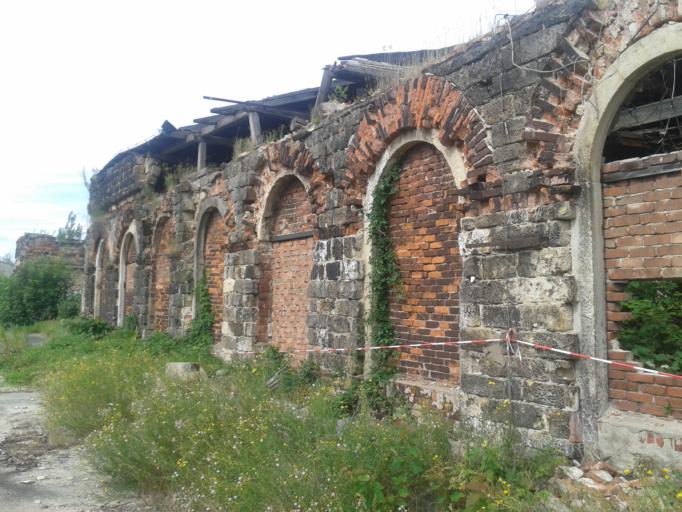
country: DE
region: Saxony
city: Dresden
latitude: 51.0659
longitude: 13.7377
